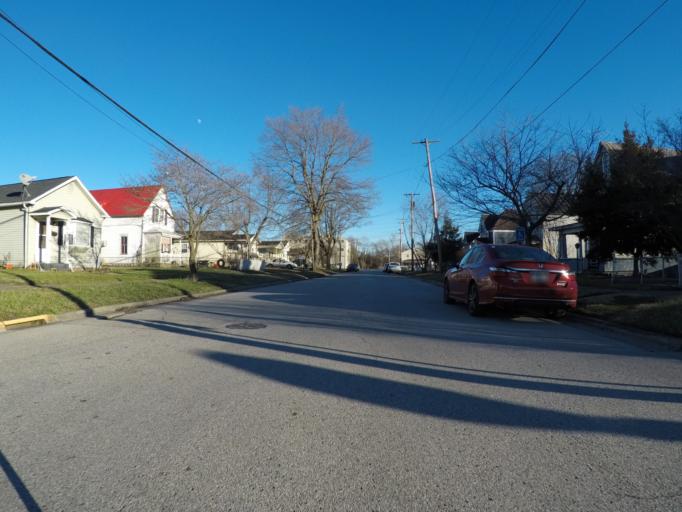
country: US
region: West Virginia
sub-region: Wayne County
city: Kenova
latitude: 38.3983
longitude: -82.5813
